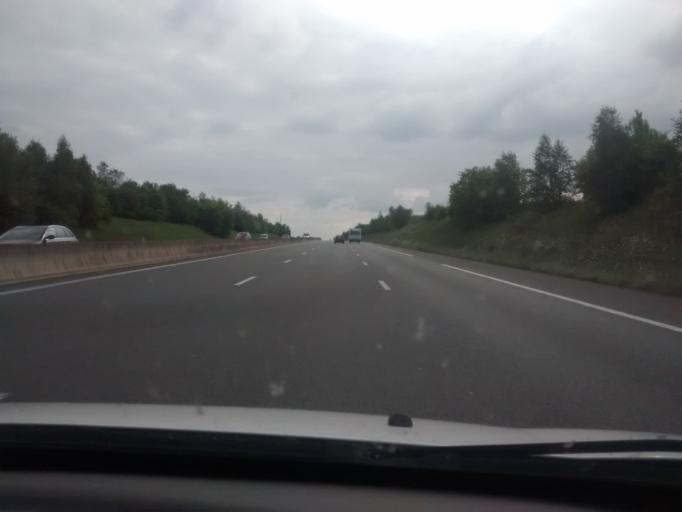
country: FR
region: Centre
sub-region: Departement d'Eure-et-Loir
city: Brou
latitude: 48.2644
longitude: 1.1457
